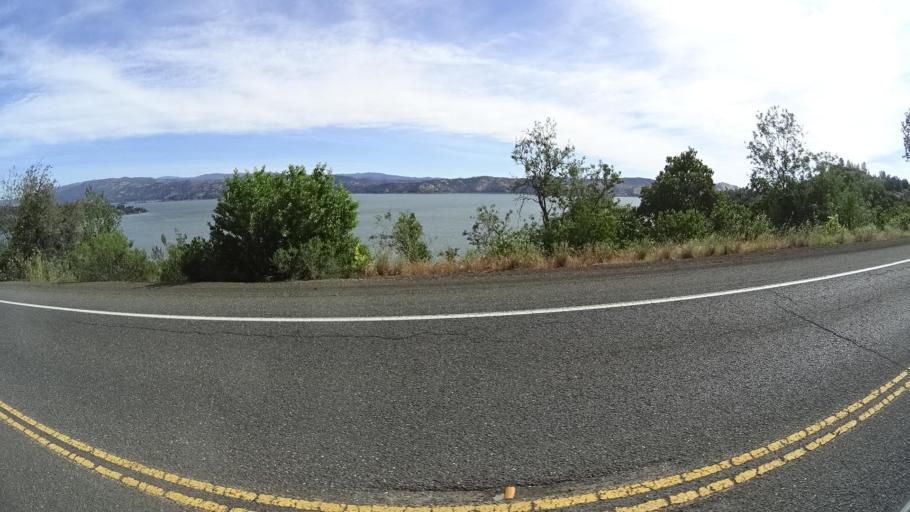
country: US
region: California
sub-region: Lake County
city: Soda Bay
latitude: 38.9619
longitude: -122.7324
